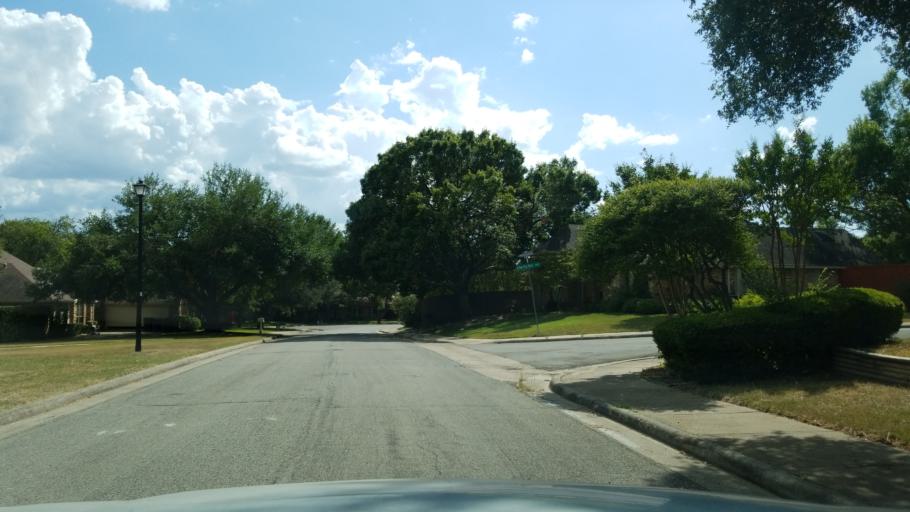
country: US
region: Texas
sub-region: Dallas County
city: Addison
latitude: 32.9550
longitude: -96.7982
